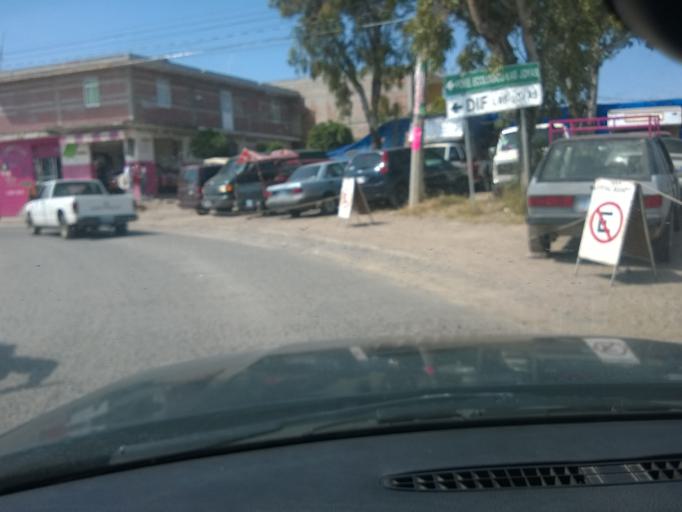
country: MX
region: Guanajuato
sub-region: Leon
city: Centro Familiar la Soledad
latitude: 21.1366
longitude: -101.7453
